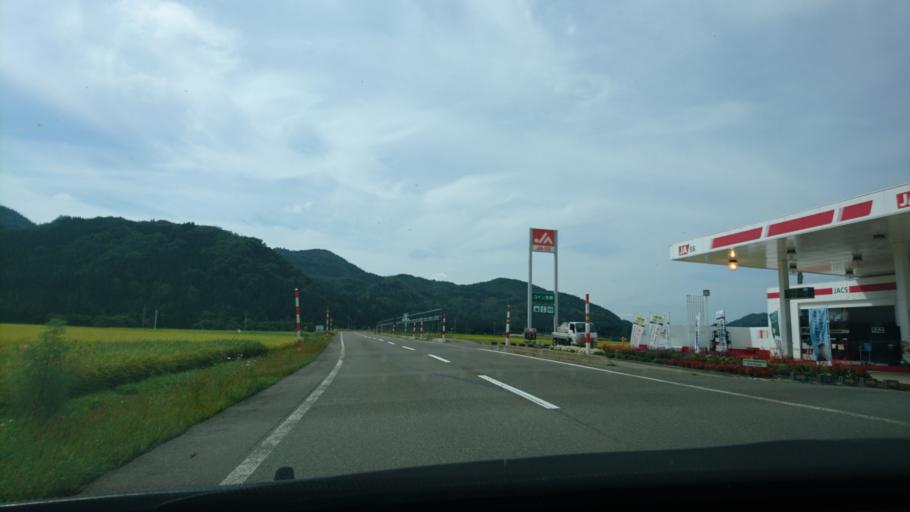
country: JP
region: Akita
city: Yuzawa
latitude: 39.1887
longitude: 140.6257
